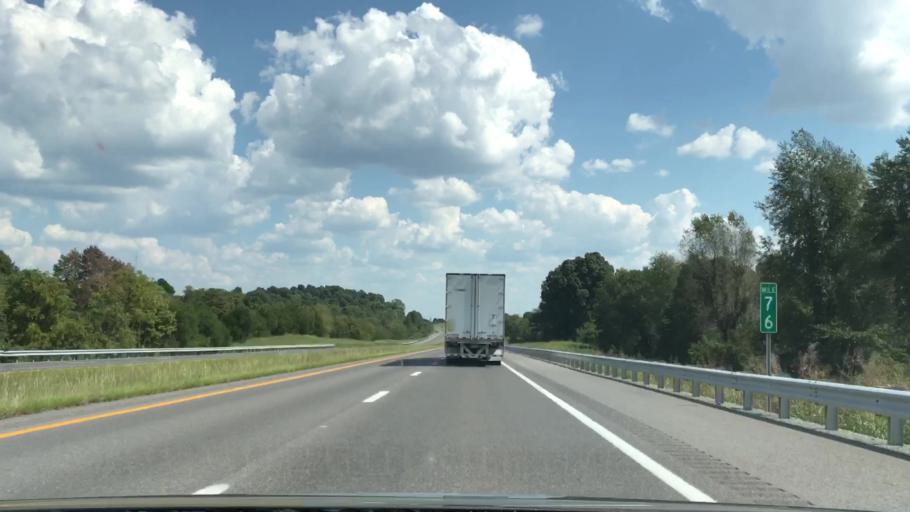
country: US
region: Kentucky
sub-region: Caldwell County
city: Princeton
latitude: 37.1105
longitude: -87.9603
